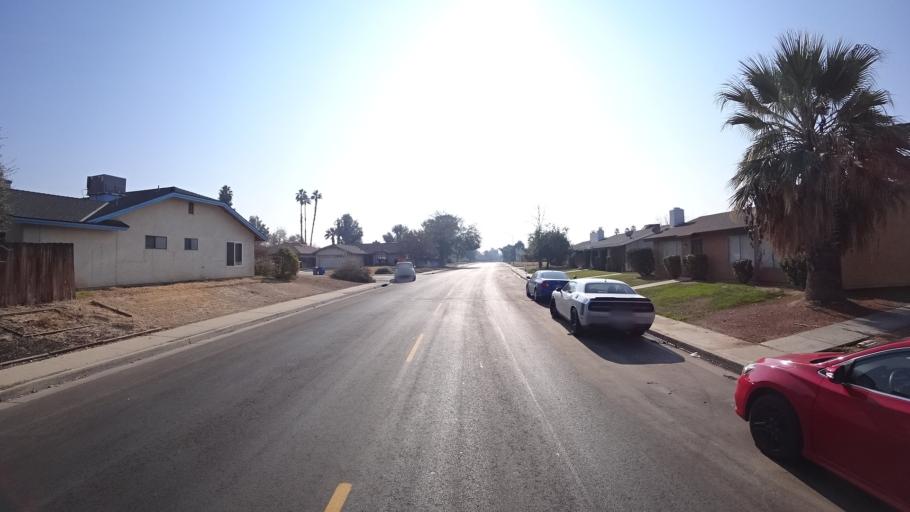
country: US
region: California
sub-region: Kern County
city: Bakersfield
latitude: 35.3268
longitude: -119.0695
